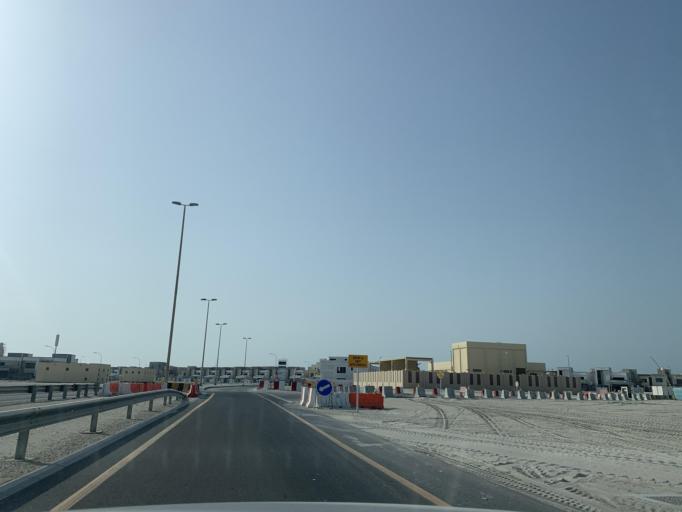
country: BH
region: Muharraq
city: Al Muharraq
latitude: 26.3200
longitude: 50.6301
